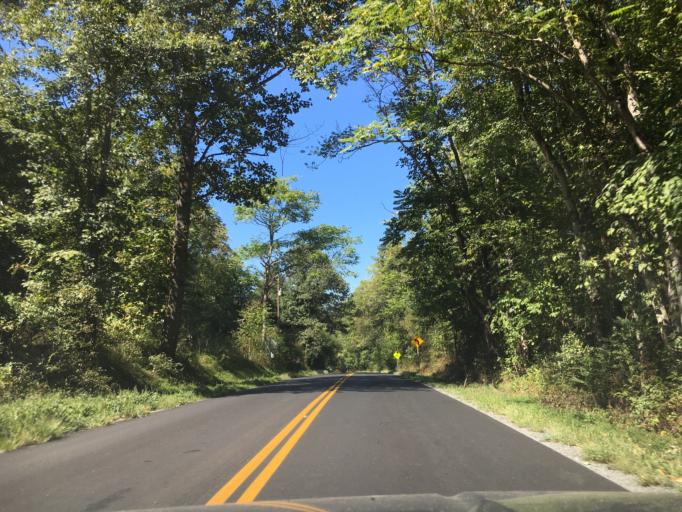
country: US
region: Virginia
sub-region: Albemarle County
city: Crozet
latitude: 37.9829
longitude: -78.7103
